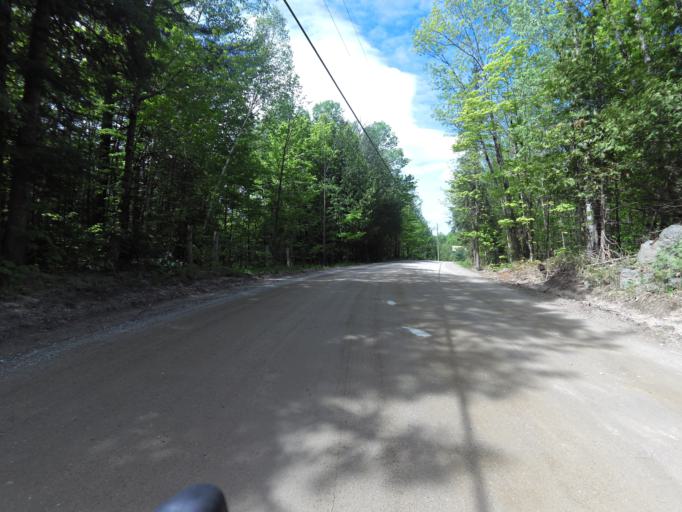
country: CA
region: Quebec
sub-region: Outaouais
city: Wakefield
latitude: 45.7834
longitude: -75.9876
